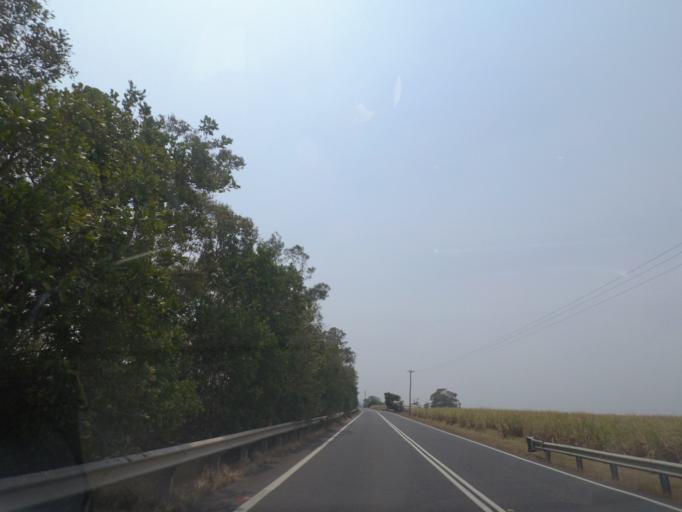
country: AU
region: New South Wales
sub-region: Richmond Valley
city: Evans Head
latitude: -28.9829
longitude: 153.4621
